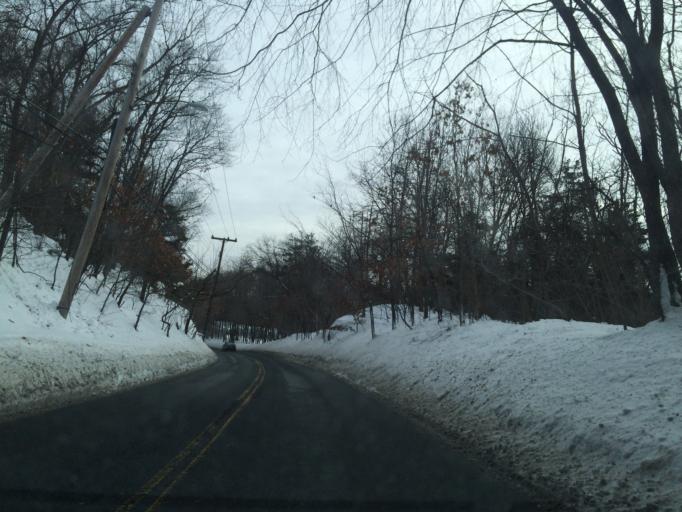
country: US
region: Massachusetts
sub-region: Middlesex County
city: Weston
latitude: 42.3382
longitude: -71.2877
